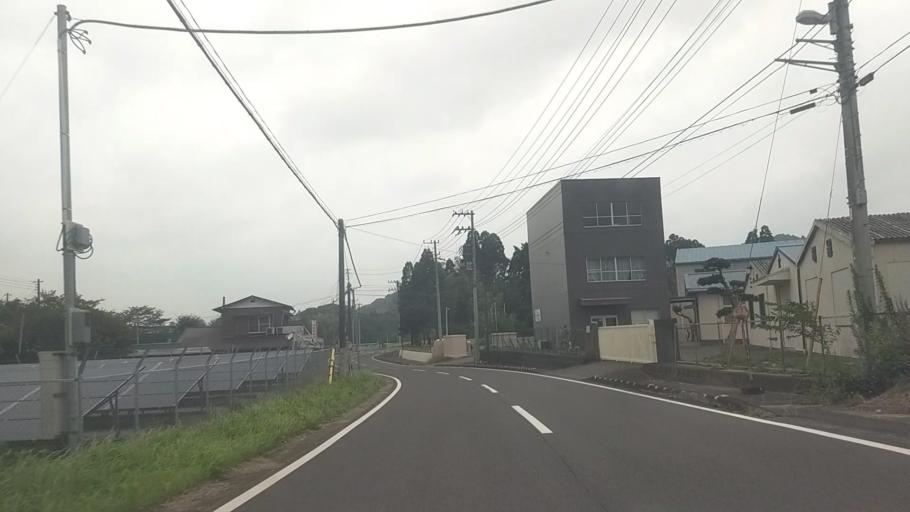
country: JP
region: Chiba
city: Ohara
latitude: 35.2652
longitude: 140.2547
